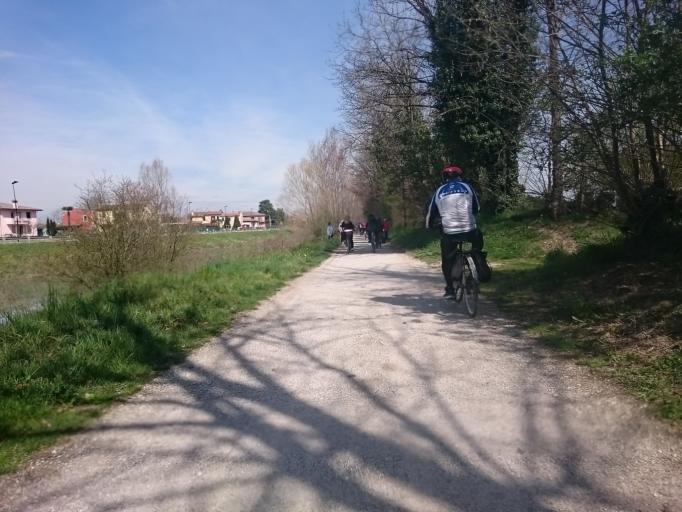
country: IT
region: Veneto
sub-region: Provincia di Padova
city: Taggi
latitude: 45.4559
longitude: 11.8331
